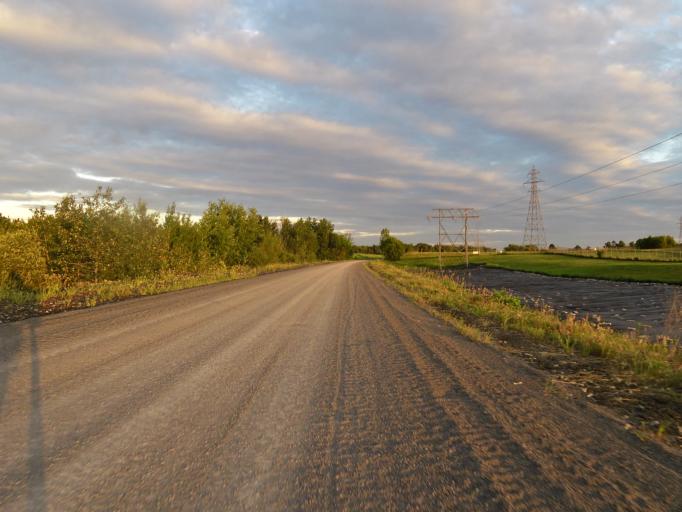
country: CA
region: Ontario
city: Arnprior
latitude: 45.4016
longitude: -76.3242
